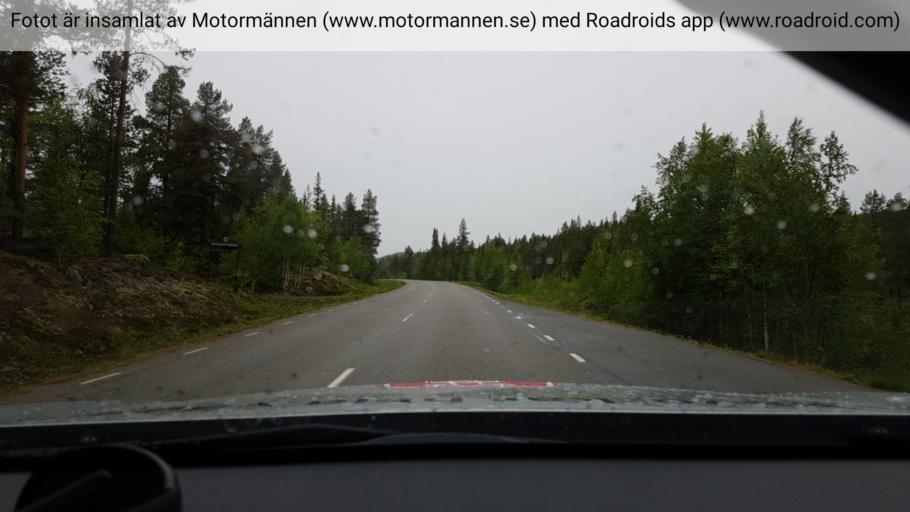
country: SE
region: Vaesterbotten
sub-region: Storumans Kommun
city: Fristad
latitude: 65.8424
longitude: 16.5932
